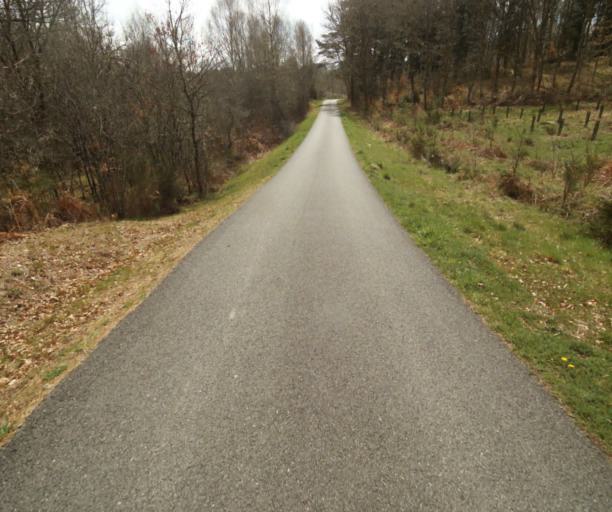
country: FR
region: Limousin
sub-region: Departement de la Correze
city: Egletons
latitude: 45.3707
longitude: 1.9684
